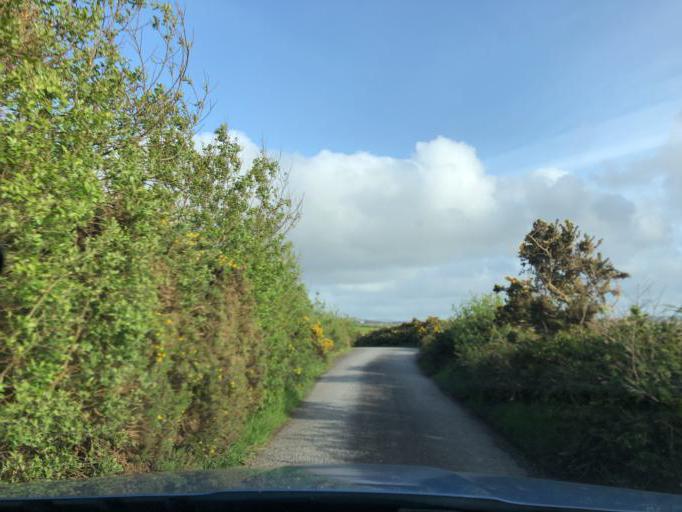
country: IE
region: Munster
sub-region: Ciarrai
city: Cahersiveen
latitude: 51.9502
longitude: -10.2609
